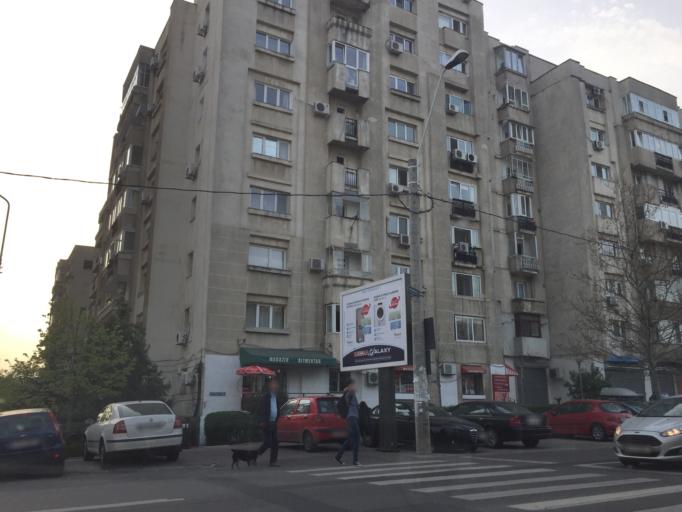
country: RO
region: Bucuresti
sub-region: Municipiul Bucuresti
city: Bucharest
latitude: 44.4221
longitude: 26.1119
